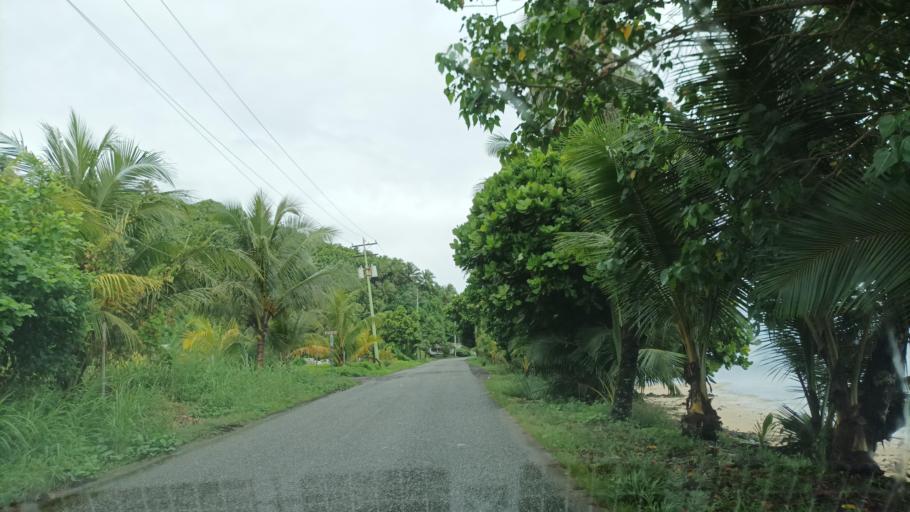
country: FM
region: Kosrae
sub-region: Tafunsak Municipality
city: Tafunsak
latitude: 5.3692
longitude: 162.9994
